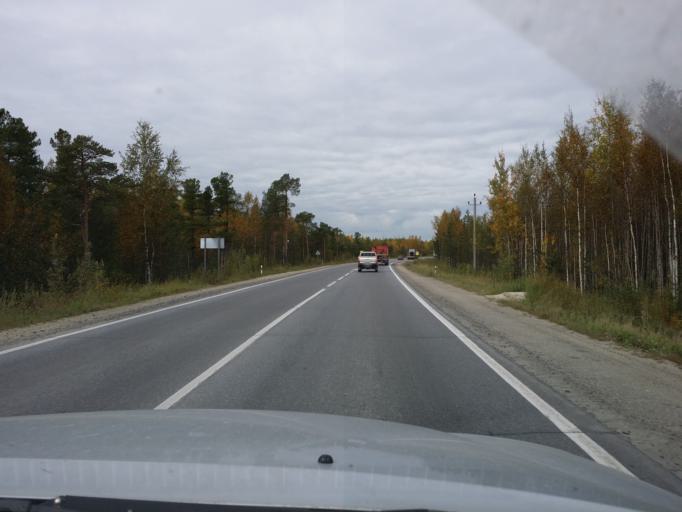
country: RU
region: Khanty-Mansiyskiy Avtonomnyy Okrug
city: Langepas
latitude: 61.1582
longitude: 75.6133
